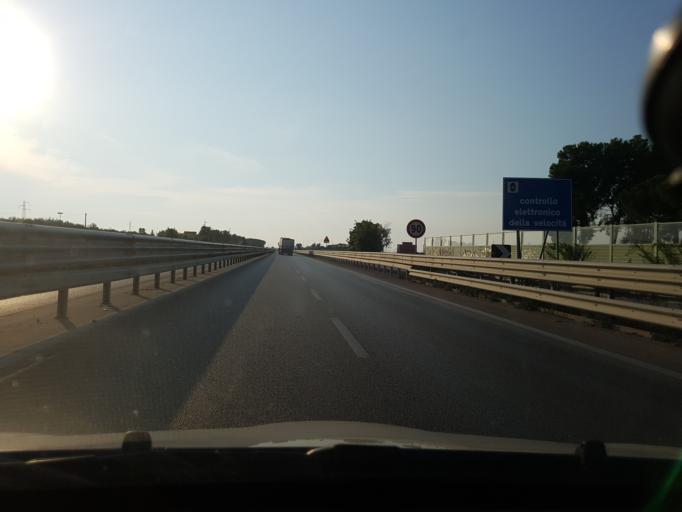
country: IT
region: Apulia
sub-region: Provincia di Foggia
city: Stornara
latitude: 41.3221
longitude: 15.7806
